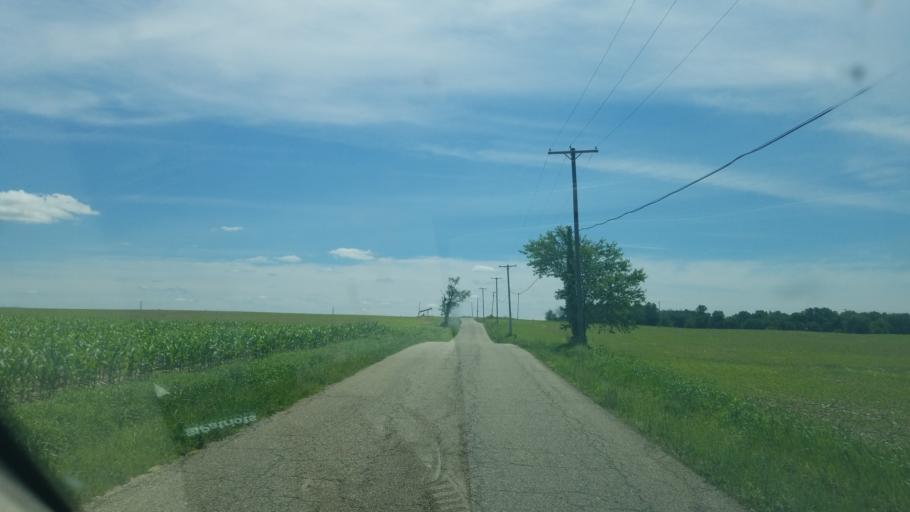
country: US
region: Ohio
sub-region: Stark County
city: Louisville
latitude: 40.8559
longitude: -81.1798
